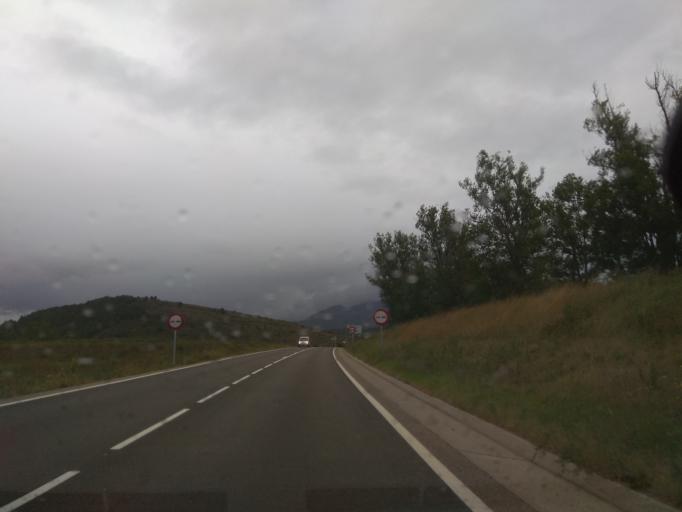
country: ES
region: Catalonia
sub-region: Provincia de Lleida
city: Bellver de Cerdanya
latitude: 42.3675
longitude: 1.7947
